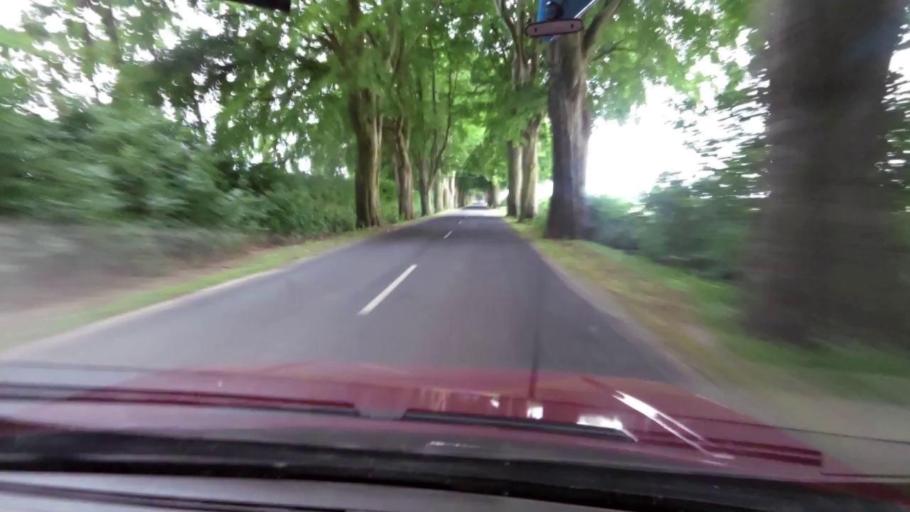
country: PL
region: West Pomeranian Voivodeship
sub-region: Powiat koszalinski
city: Polanow
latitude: 54.1407
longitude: 16.5493
